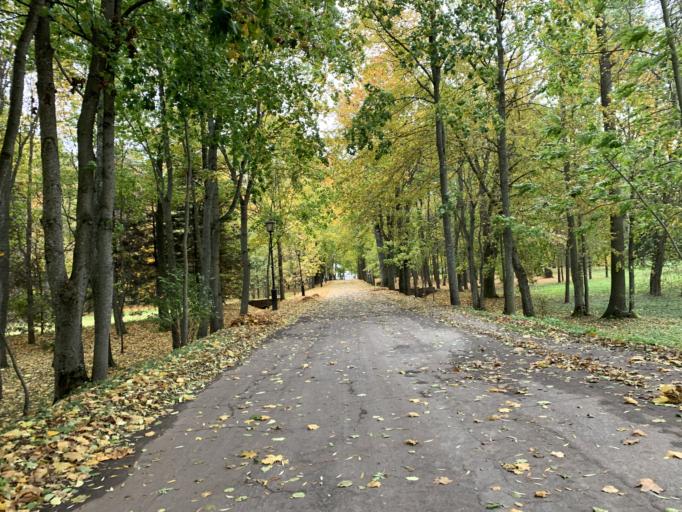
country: BY
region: Minsk
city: Nyasvizh
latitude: 53.2222
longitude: 26.6981
